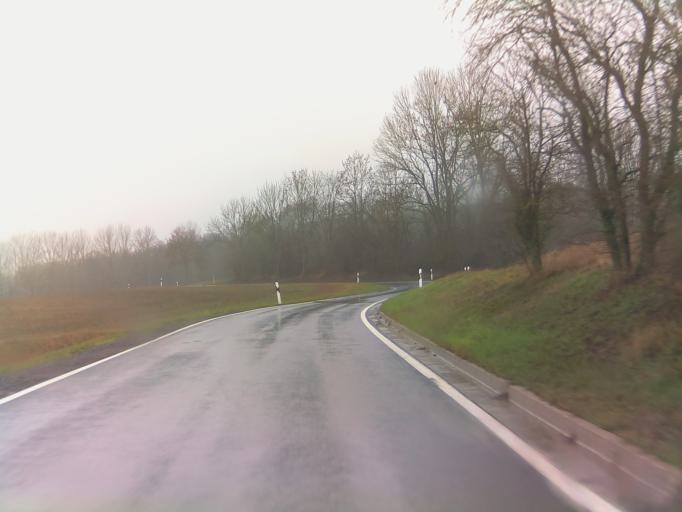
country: DE
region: Thuringia
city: Gleichamberg
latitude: 50.3933
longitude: 10.6400
